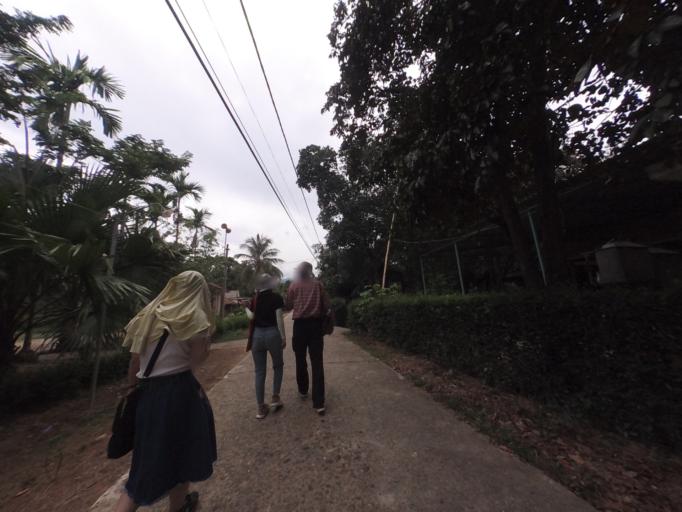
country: VN
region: Thua Thien-Hue
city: A Luoi
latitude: 16.2980
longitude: 107.3501
